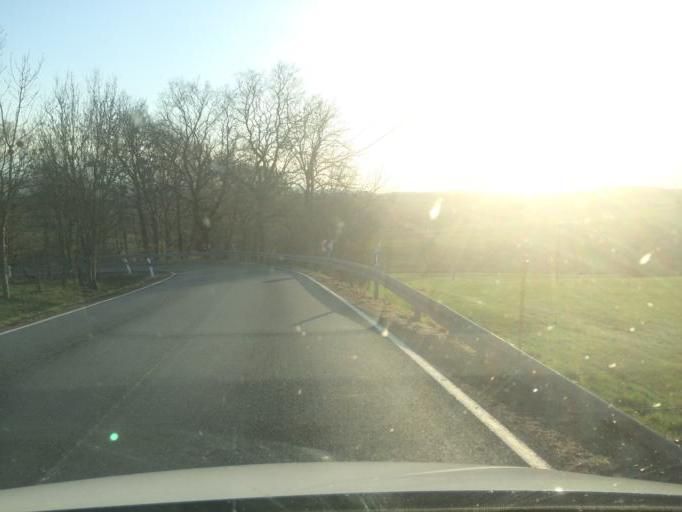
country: DE
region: Lower Saxony
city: Bad Sachsa
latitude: 51.5480
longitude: 10.5376
